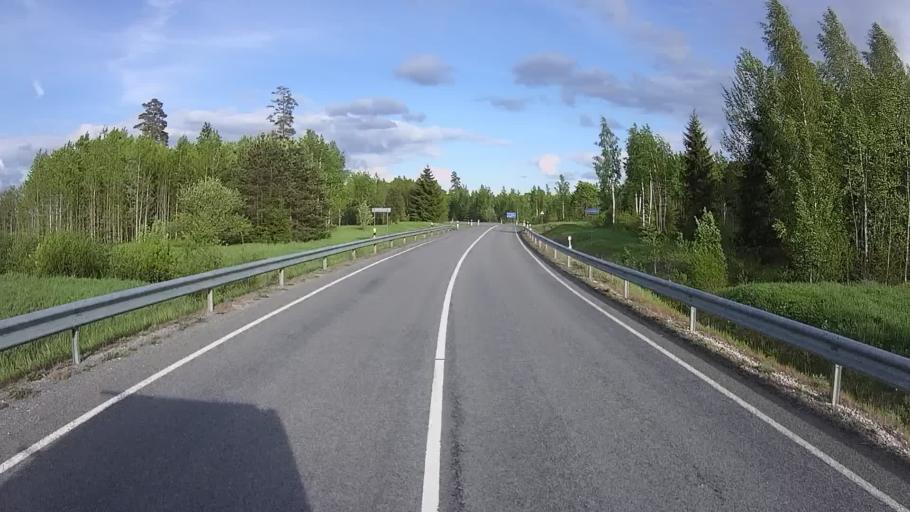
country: EE
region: Jogevamaa
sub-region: Mustvee linn
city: Mustvee
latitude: 59.0491
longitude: 27.0285
